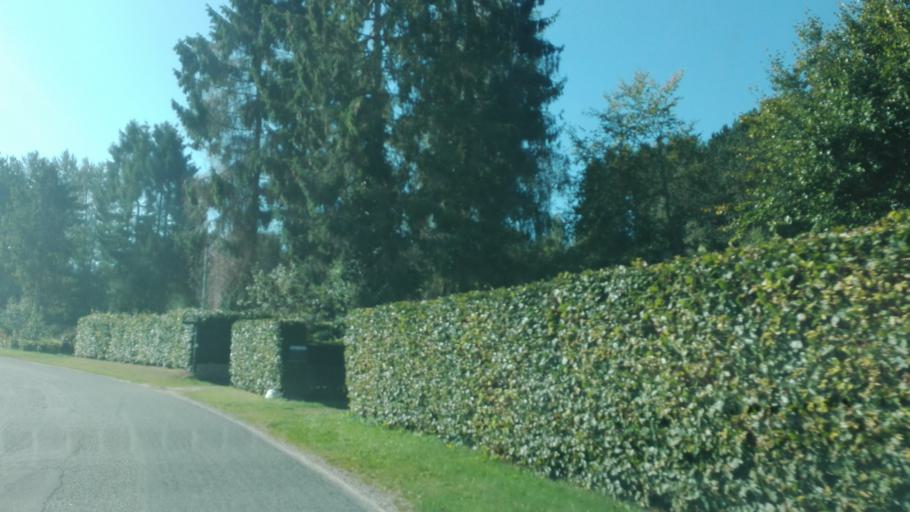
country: DK
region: Central Jutland
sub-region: Syddjurs Kommune
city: Ebeltoft
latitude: 56.2496
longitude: 10.6239
